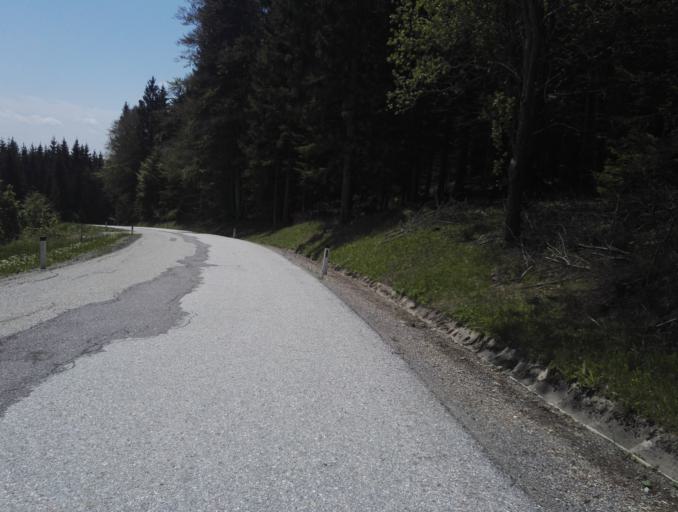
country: AT
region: Styria
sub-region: Politischer Bezirk Weiz
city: Stenzengreith
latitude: 47.2005
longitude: 15.4840
